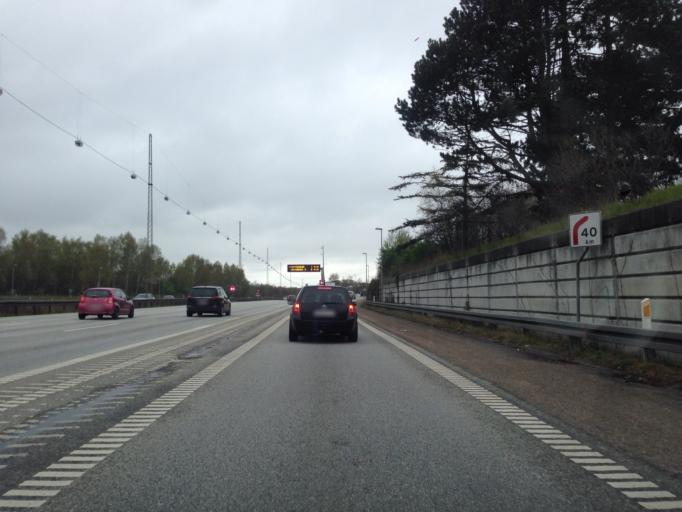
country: DK
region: Capital Region
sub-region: Rudersdal Kommune
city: Trorod
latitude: 55.8153
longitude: 12.5287
